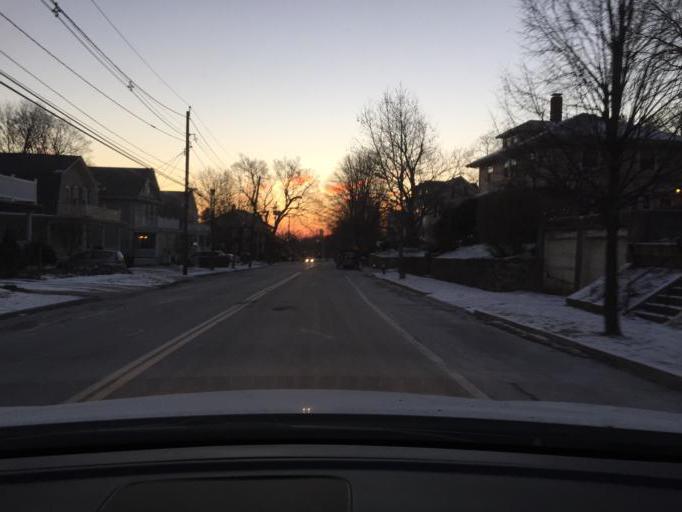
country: US
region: Massachusetts
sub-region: Middlesex County
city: Watertown
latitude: 42.3789
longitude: -71.1732
